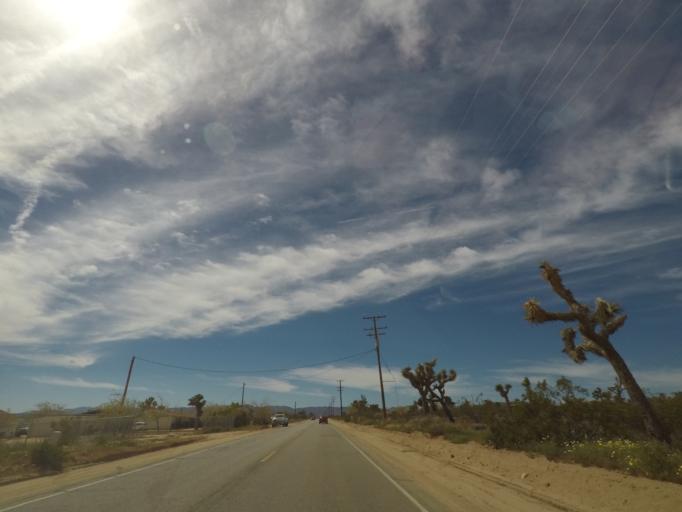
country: US
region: California
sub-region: San Bernardino County
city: Joshua Tree
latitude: 34.1845
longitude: -116.3695
